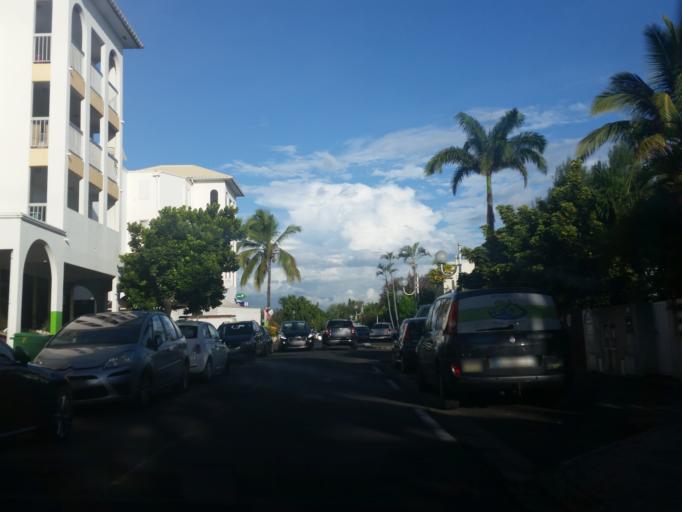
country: RE
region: Reunion
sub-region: Reunion
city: Les Avirons
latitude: -21.2725
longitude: 55.3348
